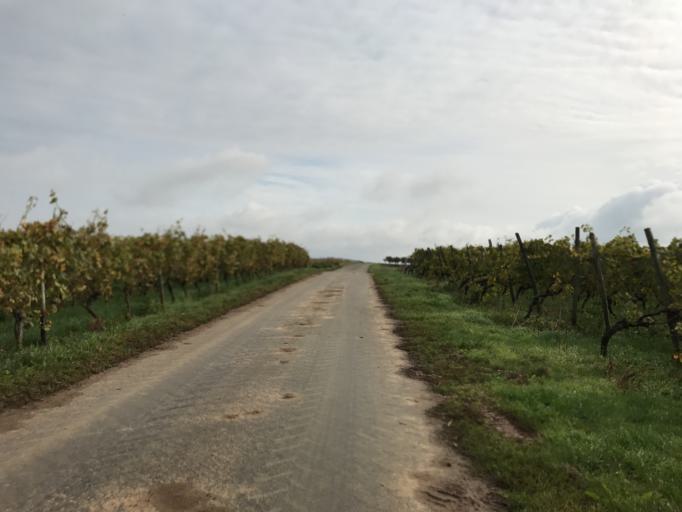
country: DE
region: Rheinland-Pfalz
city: Engelstadt
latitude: 49.9186
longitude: 8.0577
